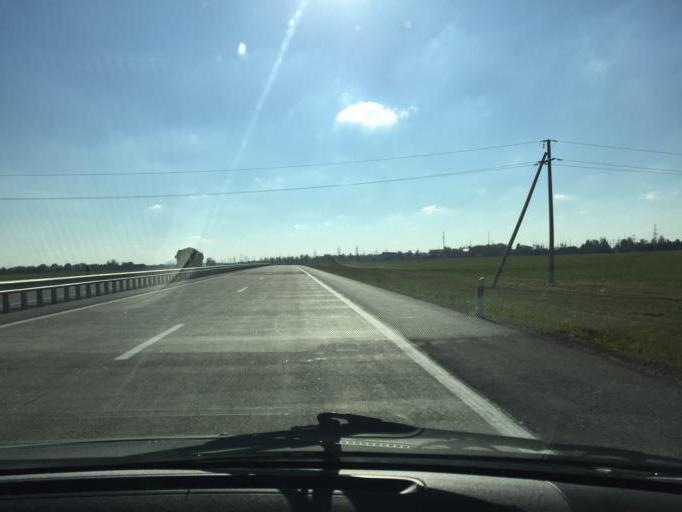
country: BY
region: Minsk
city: Slutsk
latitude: 53.0280
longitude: 27.4845
